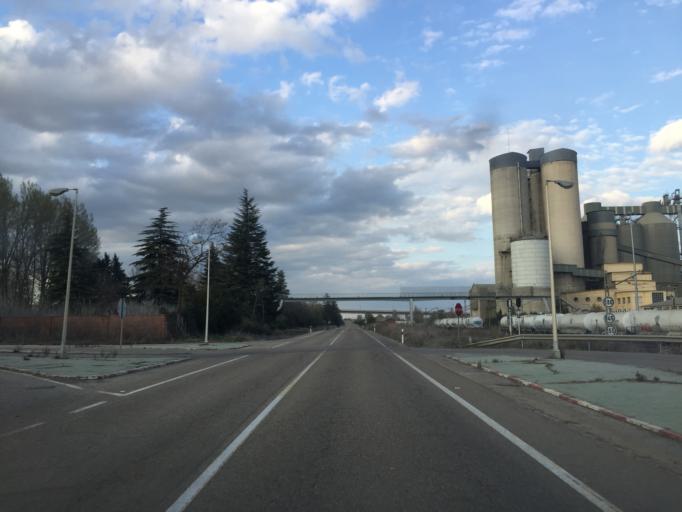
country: ES
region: Castille and Leon
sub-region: Provincia de Palencia
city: Venta de Banos
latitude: 41.9415
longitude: -4.4692
